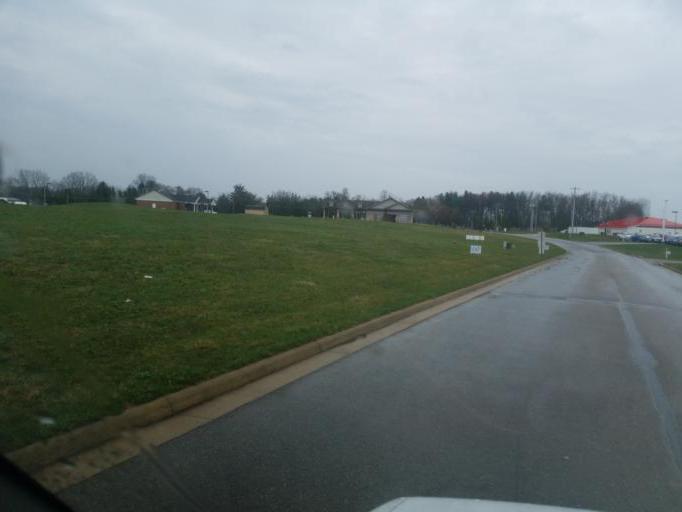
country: US
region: Ohio
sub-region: Knox County
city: Fredericktown
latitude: 40.4812
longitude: -82.5559
